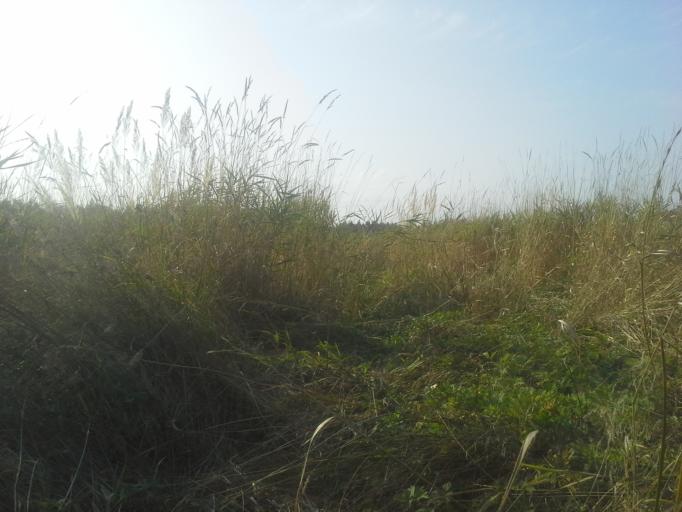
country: RU
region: Moskovskaya
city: Kievskij
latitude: 55.3818
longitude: 36.9307
